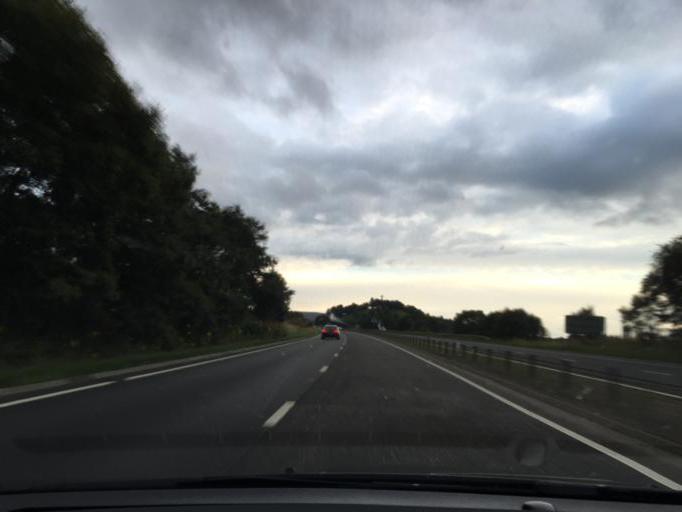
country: GB
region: Scotland
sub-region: Highland
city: Inverness
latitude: 57.4160
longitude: -4.1350
